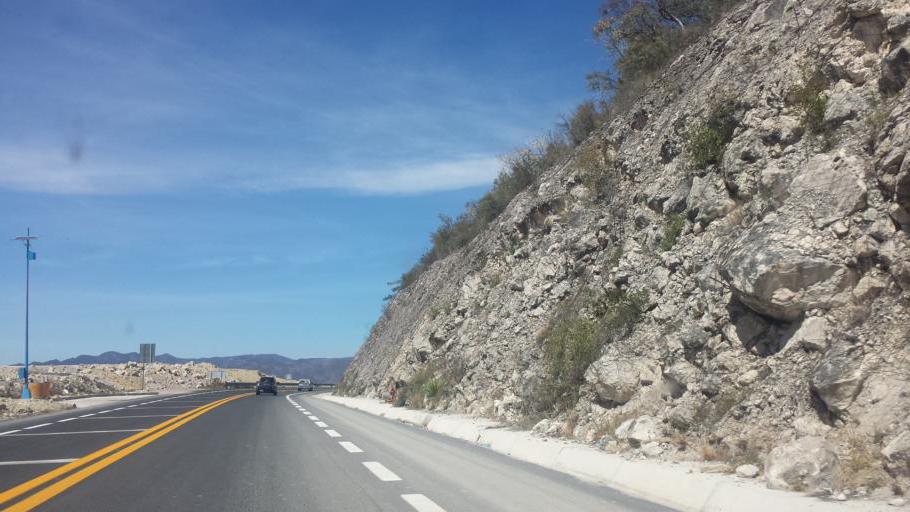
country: MX
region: Puebla
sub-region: San Jose Miahuatlan
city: San Pedro Tetitlan
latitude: 18.0554
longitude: -97.3539
